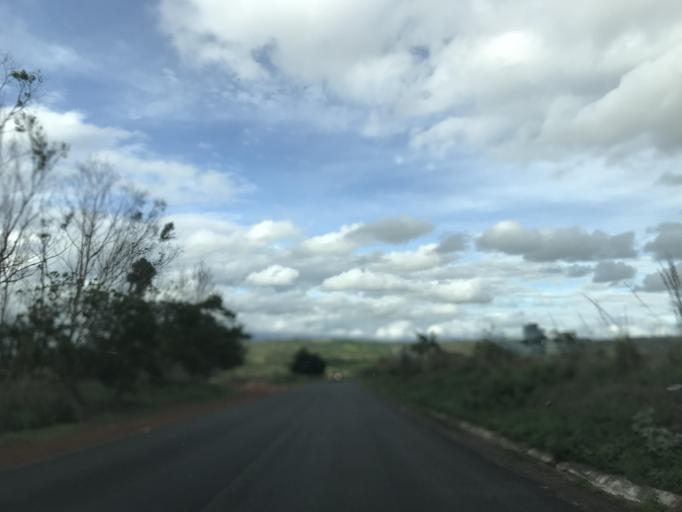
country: BR
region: Goias
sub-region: Vianopolis
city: Vianopolis
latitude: -16.9495
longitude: -48.5907
